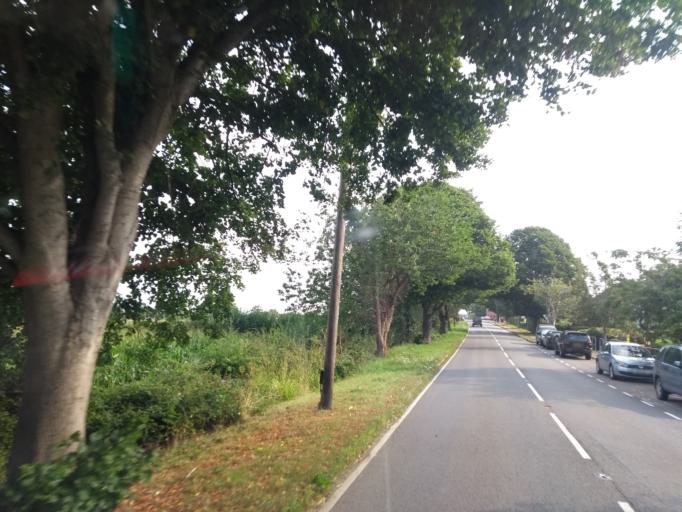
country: GB
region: England
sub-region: Devon
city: Colyton
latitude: 50.7481
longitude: -3.0314
